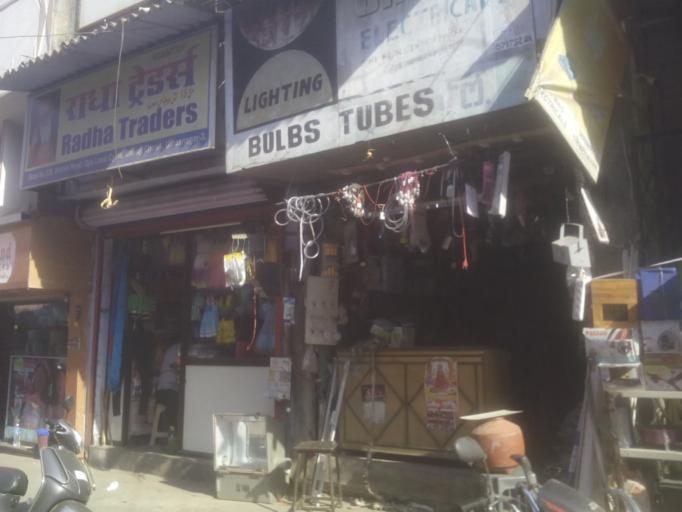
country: IN
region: Maharashtra
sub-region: Thane
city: Ulhasnagar
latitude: 19.2262
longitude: 73.1607
